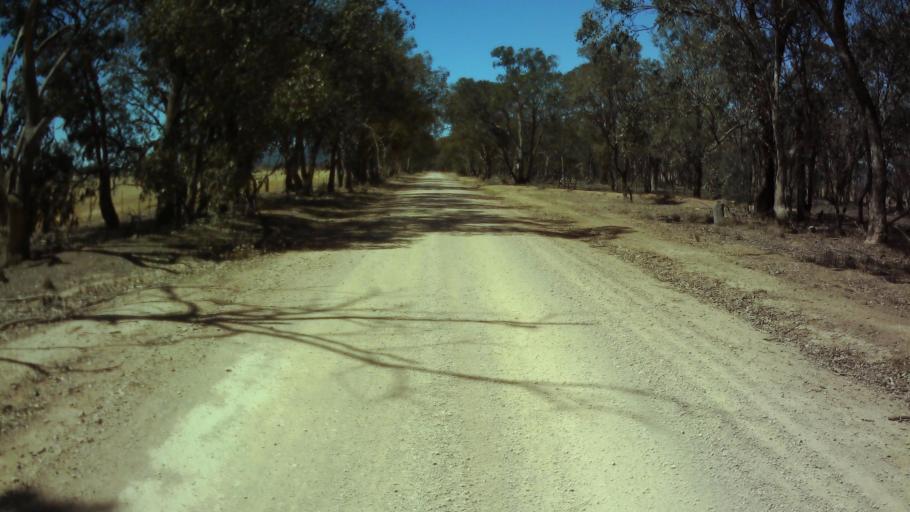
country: AU
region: New South Wales
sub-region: Weddin
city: Grenfell
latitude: -33.9160
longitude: 148.0793
